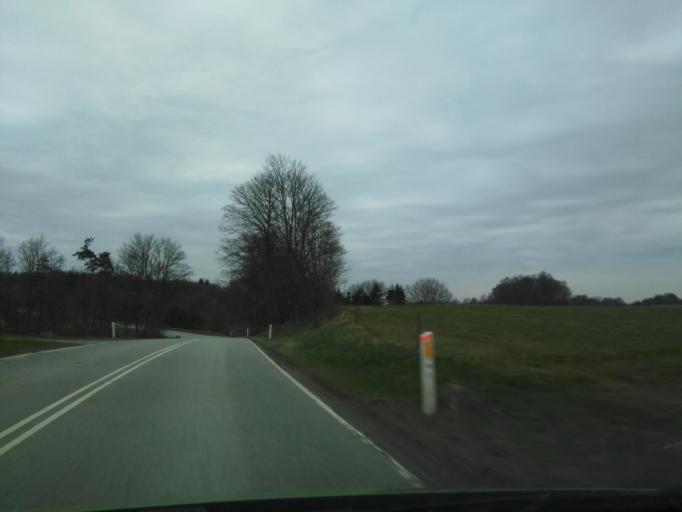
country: DK
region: North Denmark
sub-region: Mariagerfjord Kommune
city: Mariager
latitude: 56.5949
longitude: 9.9963
